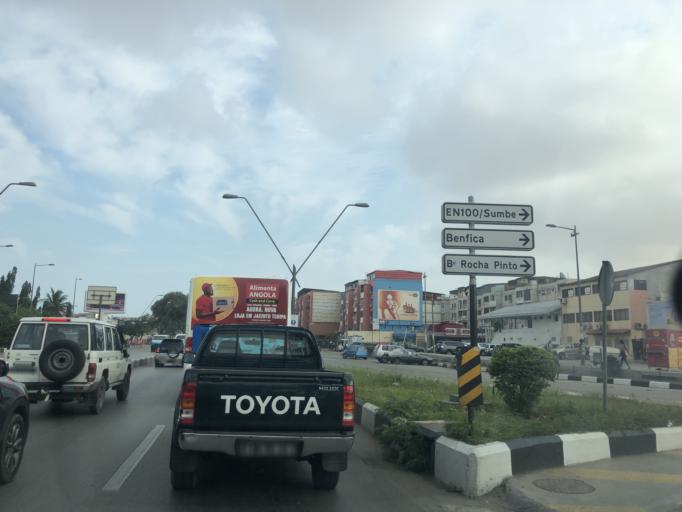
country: AO
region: Luanda
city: Luanda
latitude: -8.8454
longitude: 13.2341
